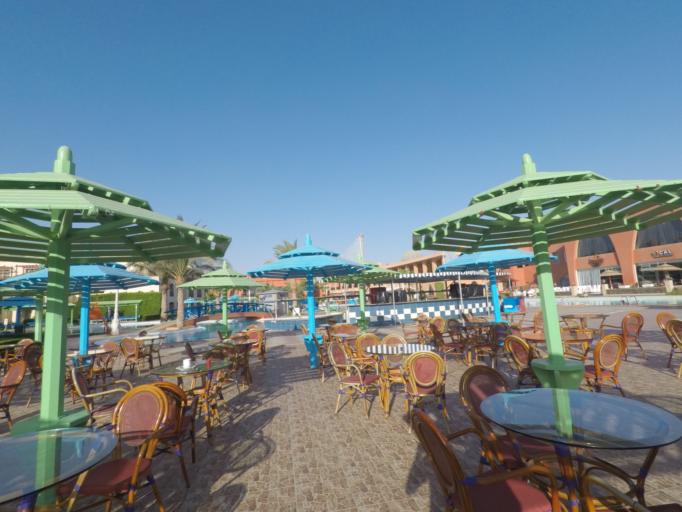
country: EG
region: Red Sea
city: Makadi Bay
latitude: 27.0900
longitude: 33.8498
